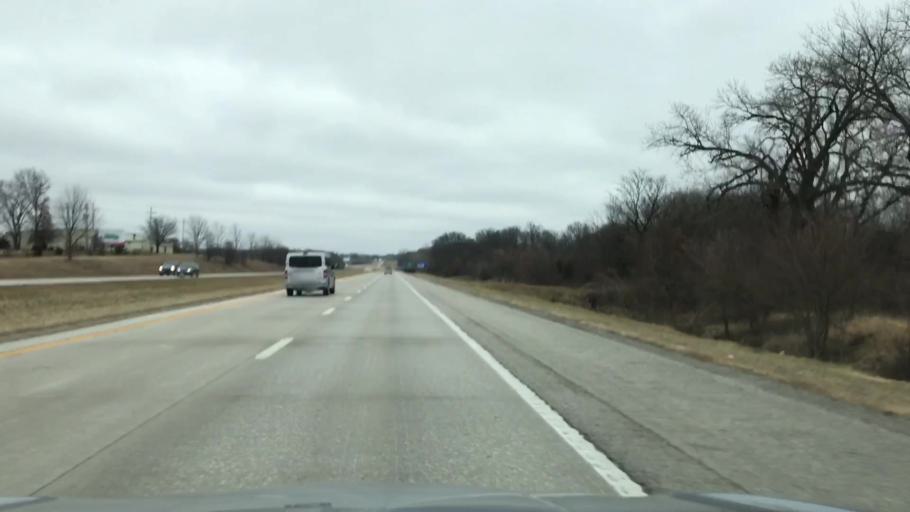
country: US
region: Missouri
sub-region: Linn County
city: Brookfield
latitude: 39.7770
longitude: -93.0946
